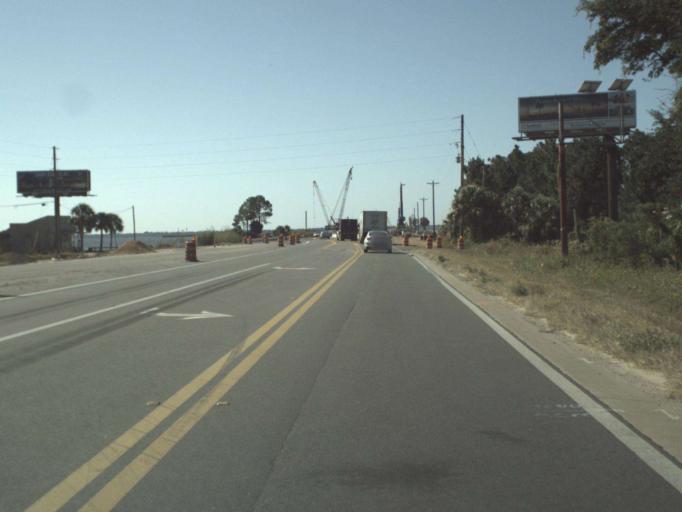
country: US
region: Florida
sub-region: Walton County
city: Freeport
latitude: 30.4325
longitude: -86.1536
